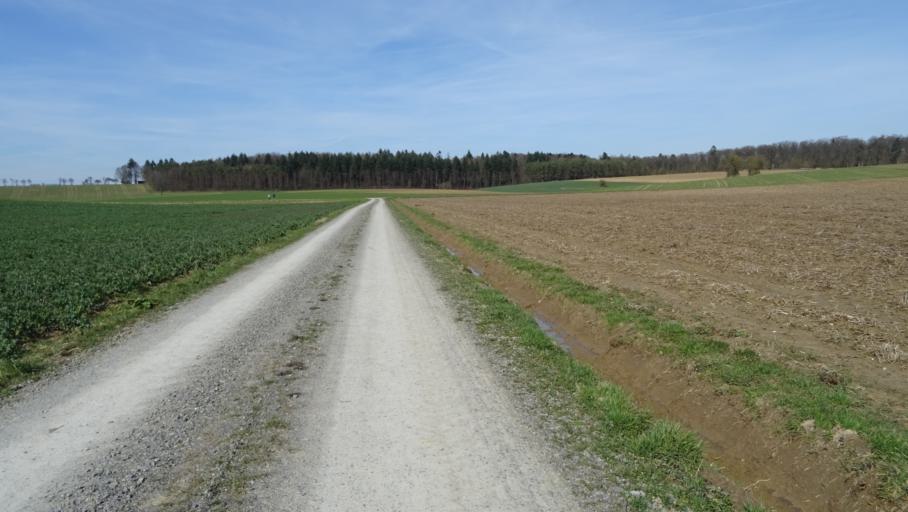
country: DE
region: Baden-Wuerttemberg
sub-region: Karlsruhe Region
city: Seckach
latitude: 49.4101
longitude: 9.3032
